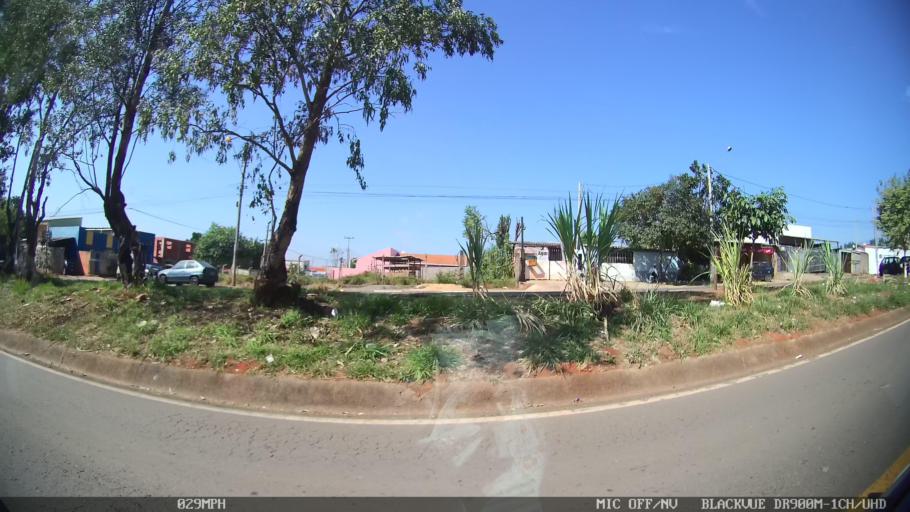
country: BR
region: Sao Paulo
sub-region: Indaiatuba
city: Indaiatuba
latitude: -23.0393
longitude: -47.1096
